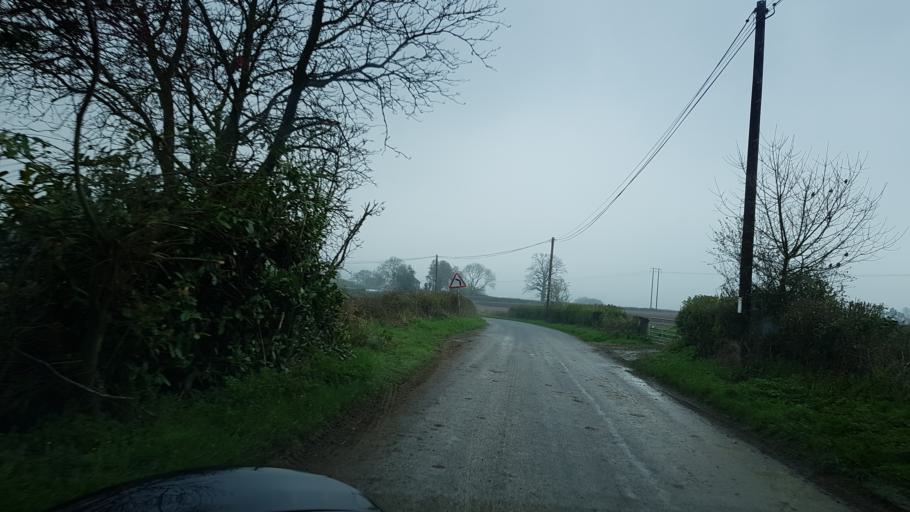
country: GB
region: England
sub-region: Herefordshire
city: Brockhampton
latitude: 52.0120
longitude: -2.5794
